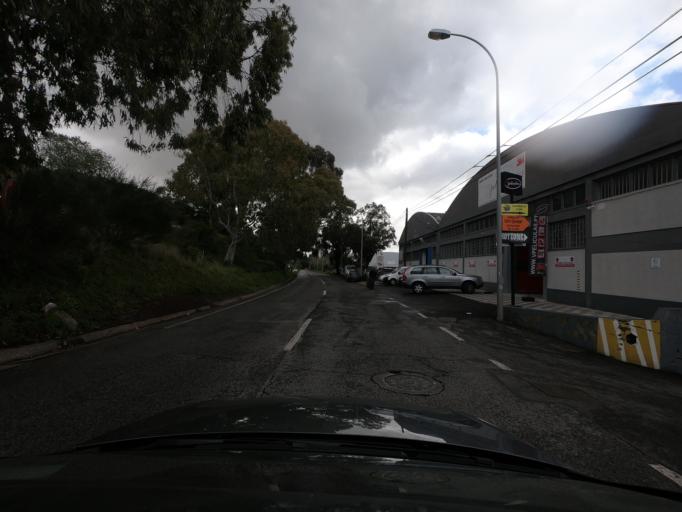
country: PT
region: Lisbon
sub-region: Oeiras
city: Quejas
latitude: 38.7313
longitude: -9.2589
